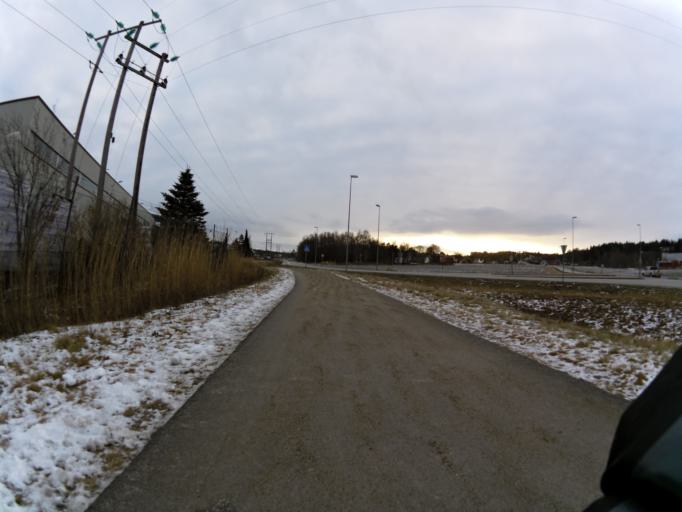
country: NO
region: Ostfold
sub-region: Fredrikstad
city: Fredrikstad
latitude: 59.2076
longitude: 10.8882
